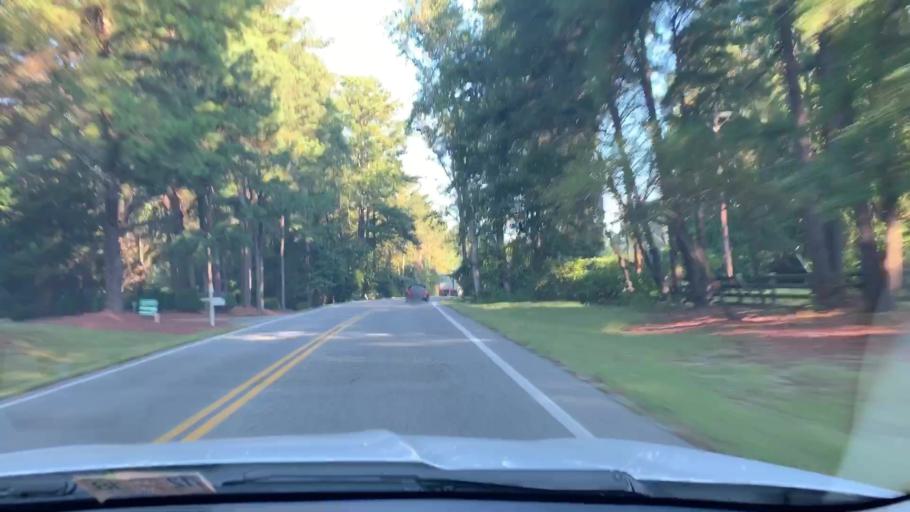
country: US
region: Virginia
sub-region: Middlesex County
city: Deltaville
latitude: 37.5210
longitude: -76.4229
